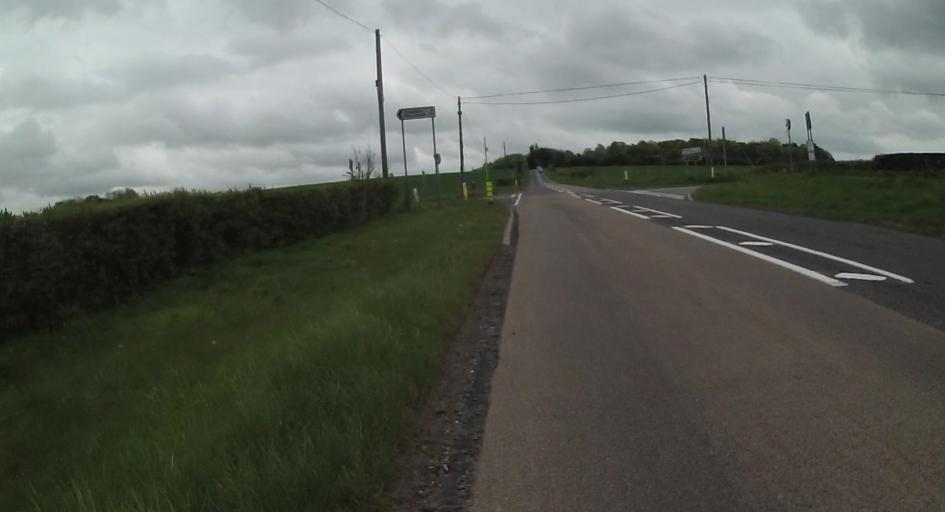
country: GB
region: England
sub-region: Hampshire
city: Colden Common
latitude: 51.0151
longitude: -1.2522
